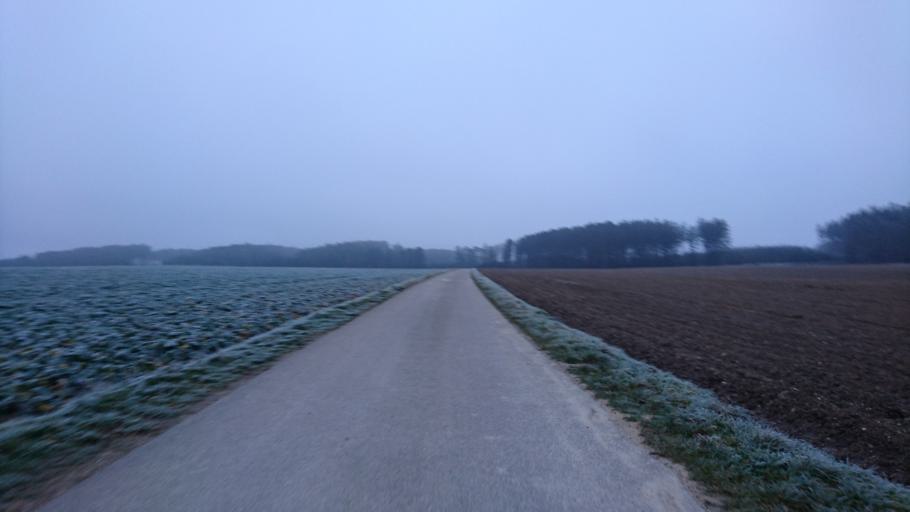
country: DE
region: Bavaria
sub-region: Swabia
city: Altenmunster
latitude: 48.4377
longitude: 10.6135
